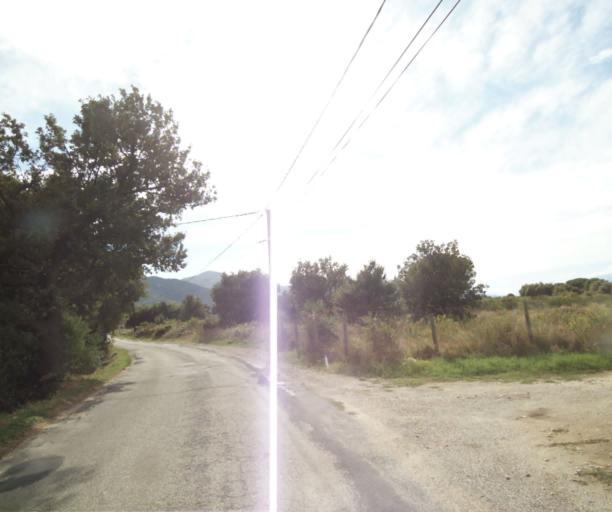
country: FR
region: Languedoc-Roussillon
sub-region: Departement des Pyrenees-Orientales
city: Sant Andreu de Sureda
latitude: 42.5441
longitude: 2.9899
